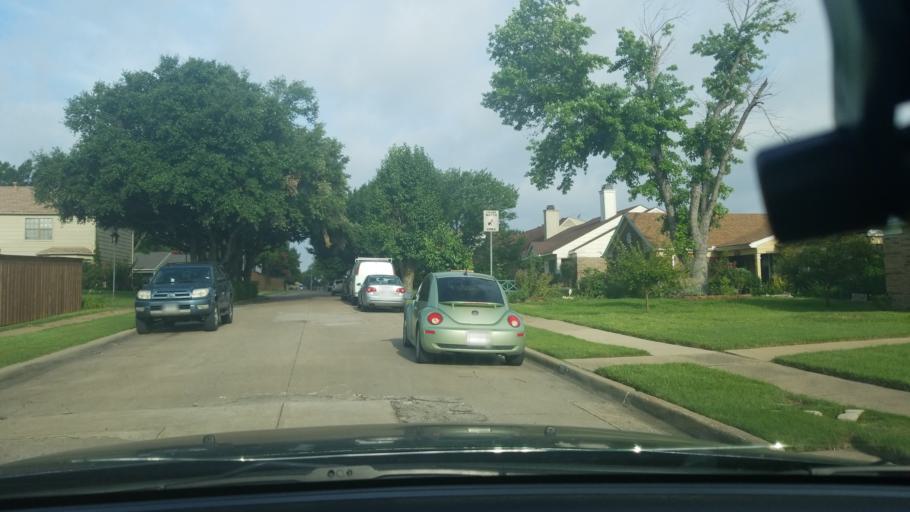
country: US
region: Texas
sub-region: Dallas County
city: Mesquite
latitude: 32.7885
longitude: -96.6474
